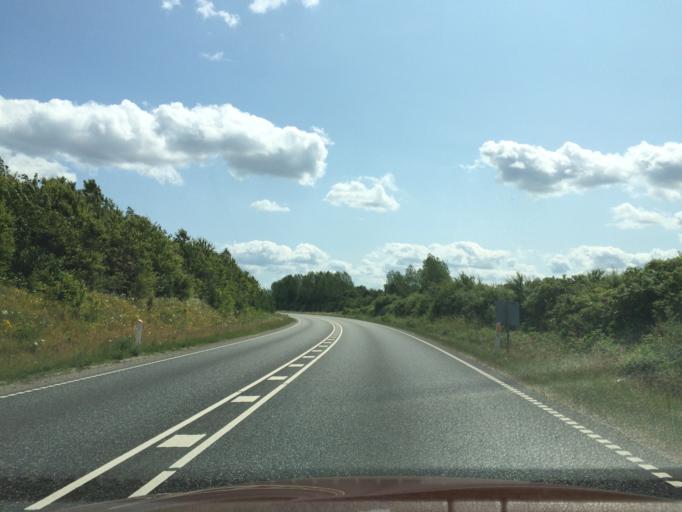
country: DK
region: Central Jutland
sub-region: Arhus Kommune
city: Sabro
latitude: 56.2011
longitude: 10.0517
